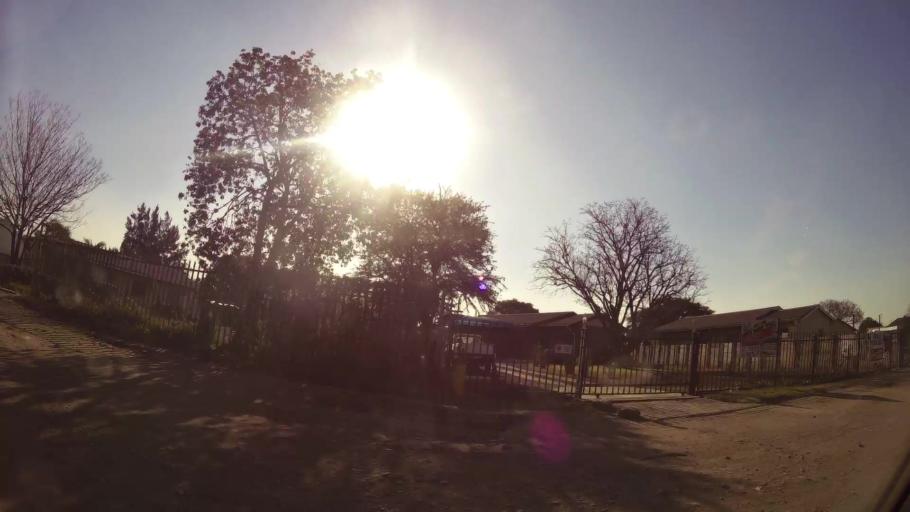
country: ZA
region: North-West
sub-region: Bojanala Platinum District Municipality
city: Rustenburg
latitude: -25.6606
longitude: 27.2656
